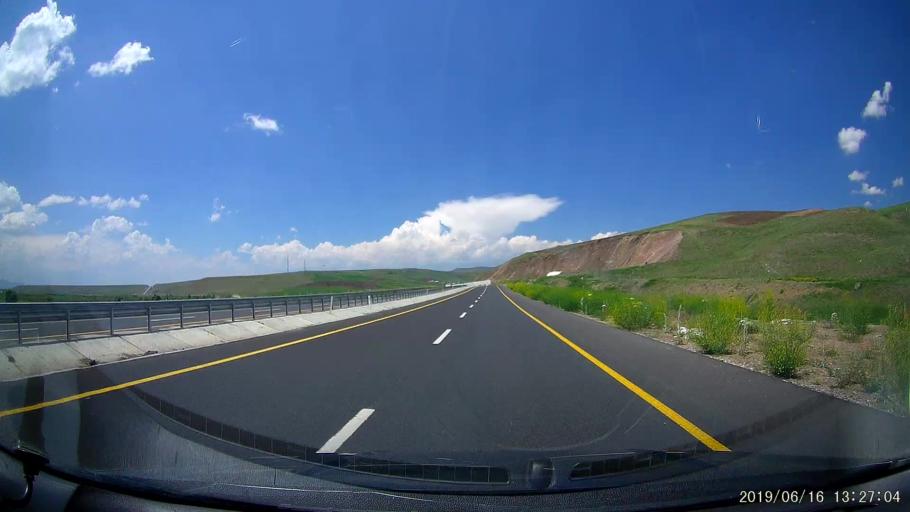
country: TR
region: Agri
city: Taslicay
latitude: 39.6662
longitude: 43.3165
